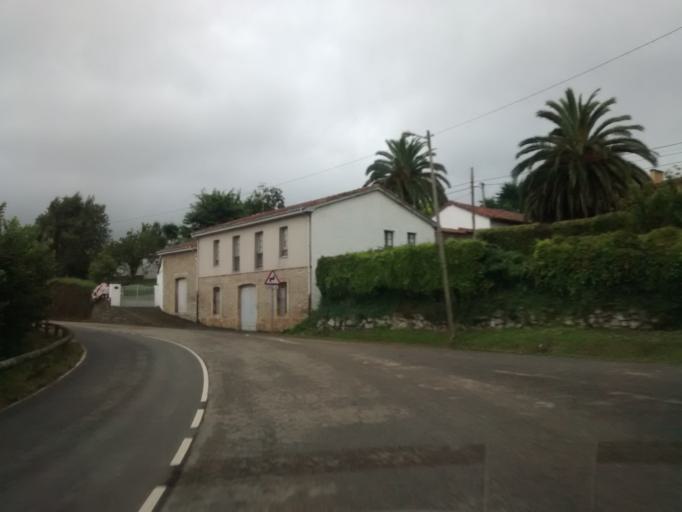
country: ES
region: Asturias
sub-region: Province of Asturias
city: Villaviciosa
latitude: 43.5201
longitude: -5.4014
